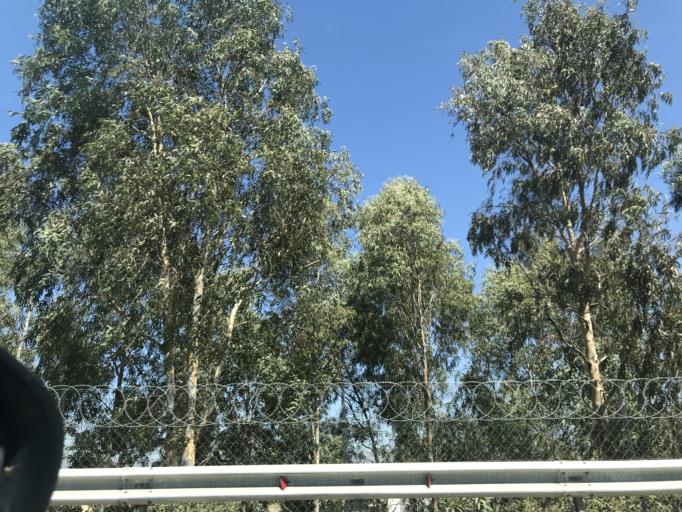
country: TR
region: Aydin
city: Aydin
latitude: 37.8245
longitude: 27.8396
